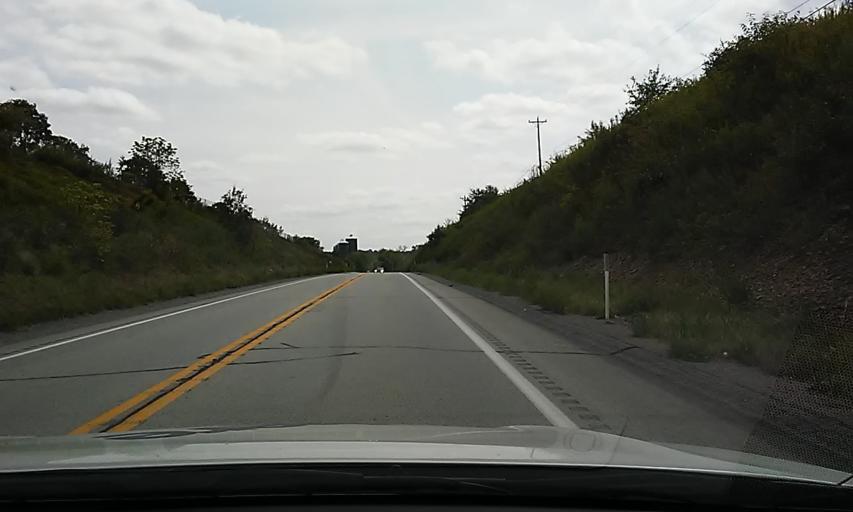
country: US
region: Pennsylvania
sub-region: Indiana County
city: Clymer
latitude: 40.7960
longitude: -79.0540
